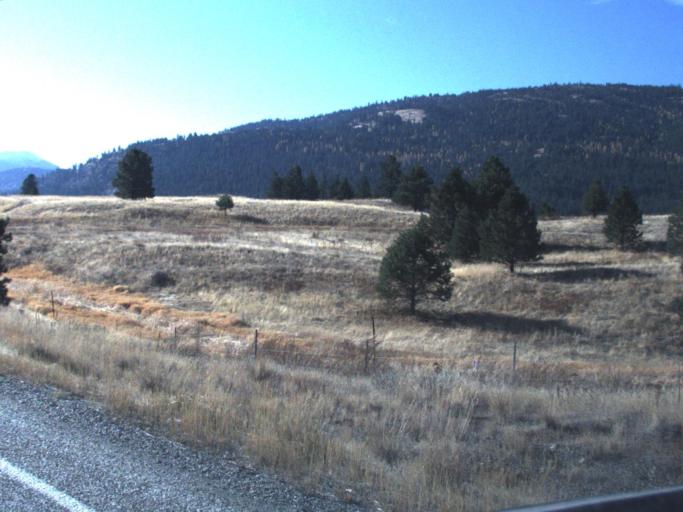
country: US
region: Washington
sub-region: Ferry County
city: Republic
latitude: 48.7084
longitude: -118.6558
